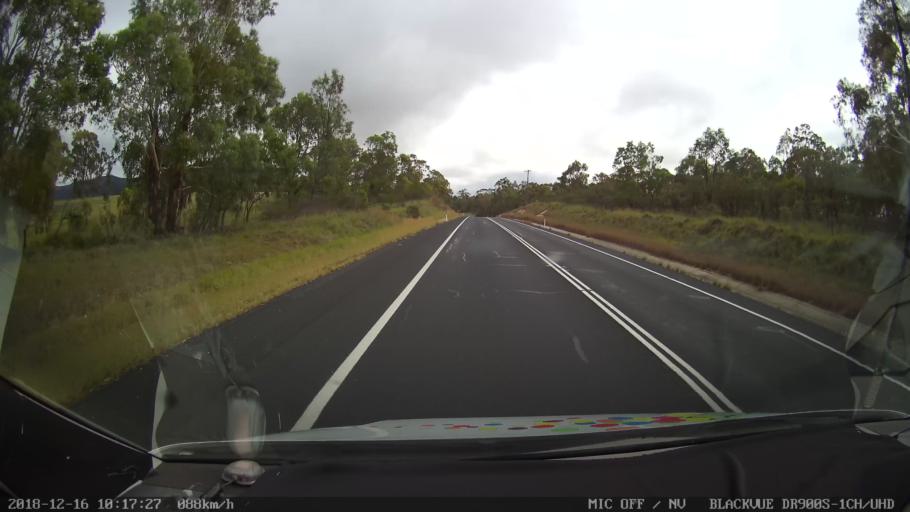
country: AU
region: New South Wales
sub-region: Tenterfield Municipality
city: Carrolls Creek
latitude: -29.2560
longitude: 151.9918
